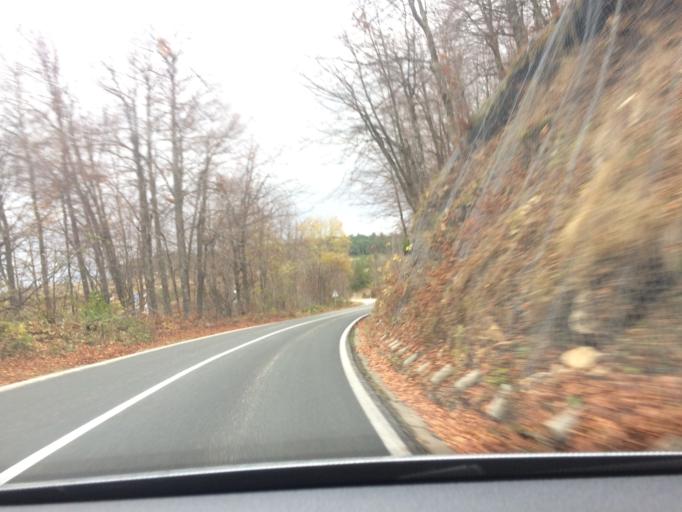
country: ME
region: Opstina Zabljak
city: Zabljak
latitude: 43.1483
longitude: 19.2435
